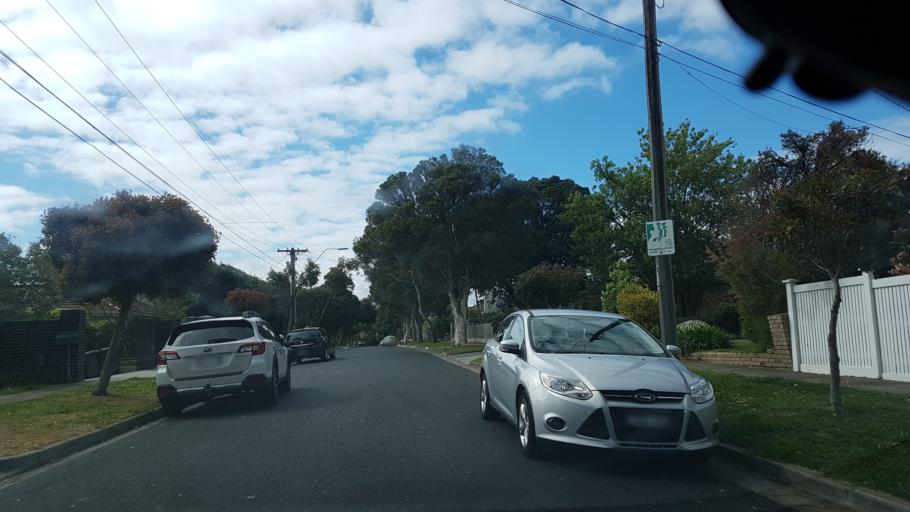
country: AU
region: Victoria
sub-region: Bayside
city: Hampton East
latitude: -37.9310
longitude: 145.0234
